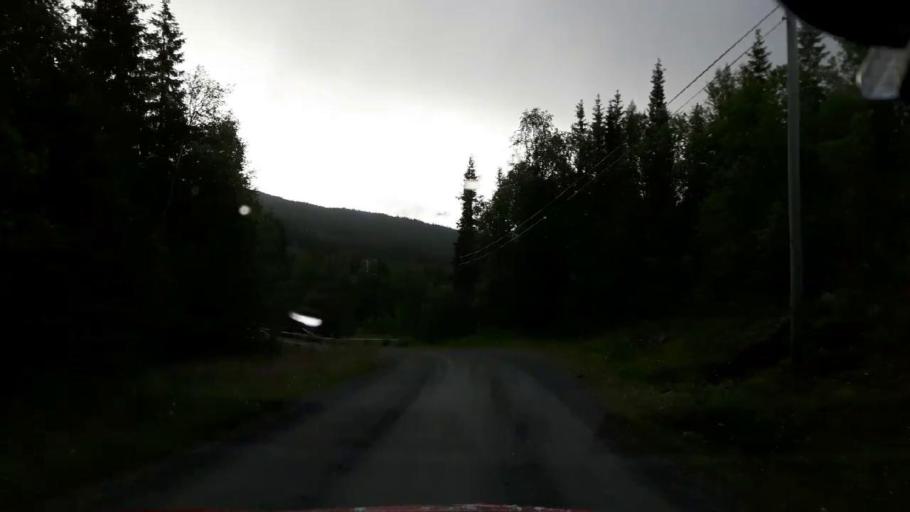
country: NO
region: Nordland
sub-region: Hattfjelldal
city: Hattfjelldal
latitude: 64.8837
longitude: 14.8448
